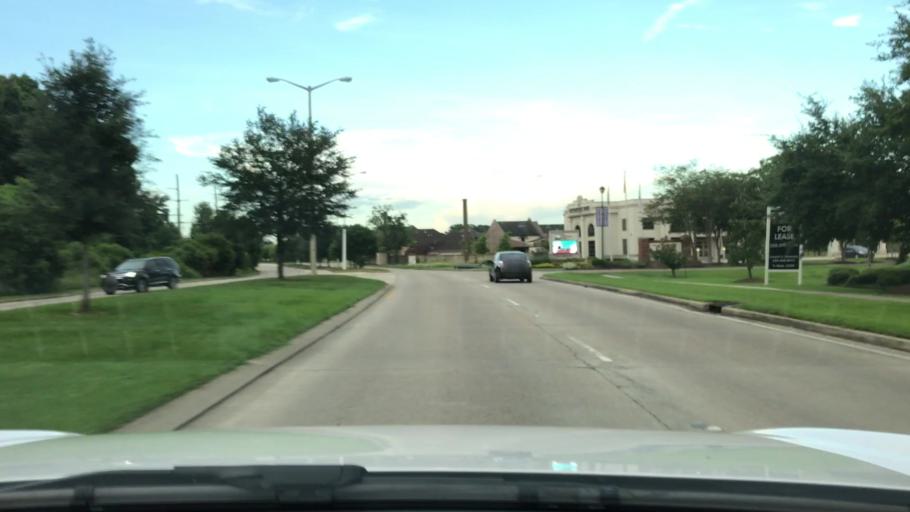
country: US
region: Louisiana
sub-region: East Baton Rouge Parish
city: Westminster
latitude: 30.4244
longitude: -91.1249
